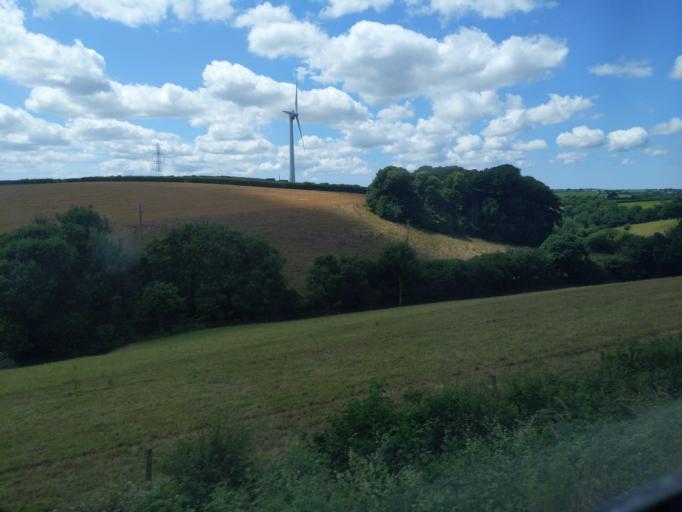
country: GB
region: England
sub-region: Cornwall
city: Liskeard
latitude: 50.4372
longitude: -4.4445
